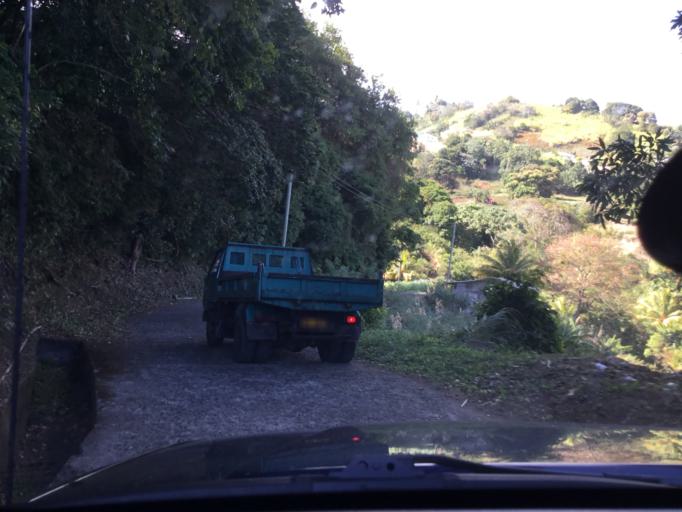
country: VC
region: Charlotte
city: Biabou
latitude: 13.1594
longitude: -61.1685
